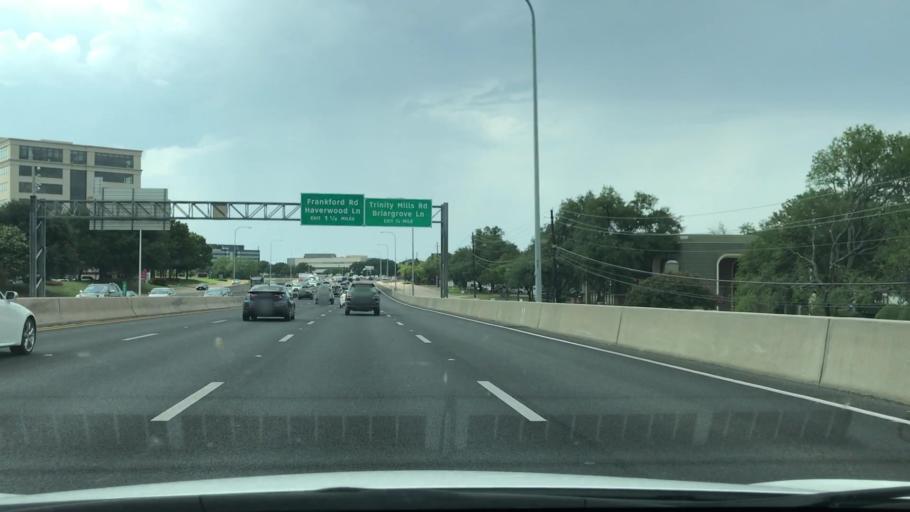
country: US
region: Texas
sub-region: Dallas County
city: Addison
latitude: 32.9760
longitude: -96.8241
